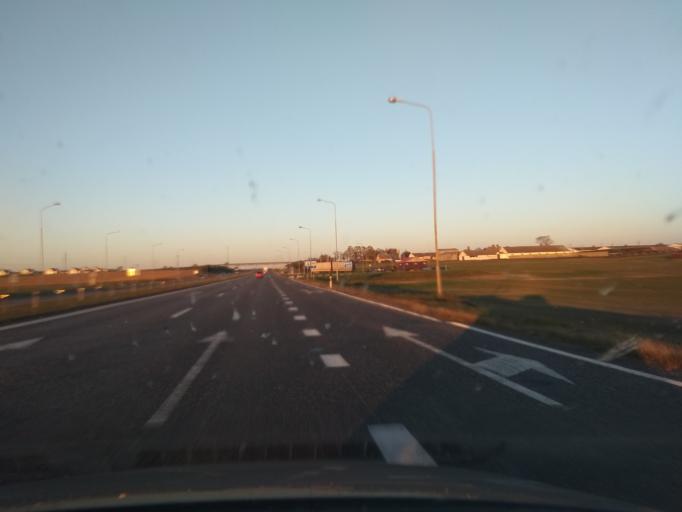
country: BY
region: Minsk
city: Haradzyeya
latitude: 53.3414
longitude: 26.4418
